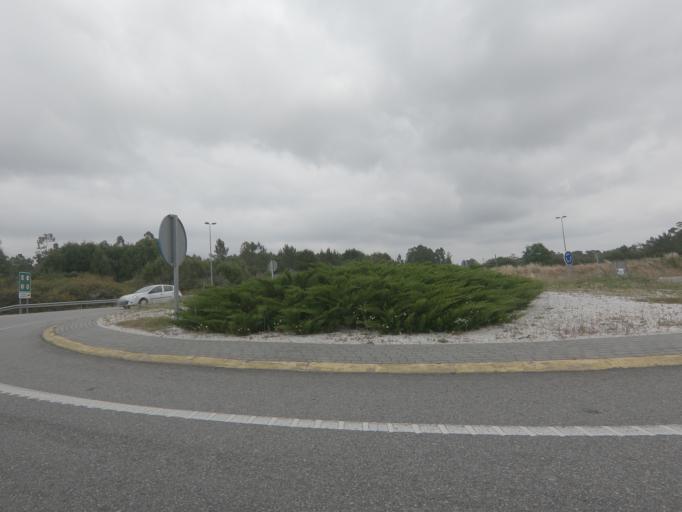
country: PT
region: Viana do Castelo
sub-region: Vila Nova de Cerveira
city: Vila Nova de Cerveira
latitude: 41.9539
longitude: -8.7669
